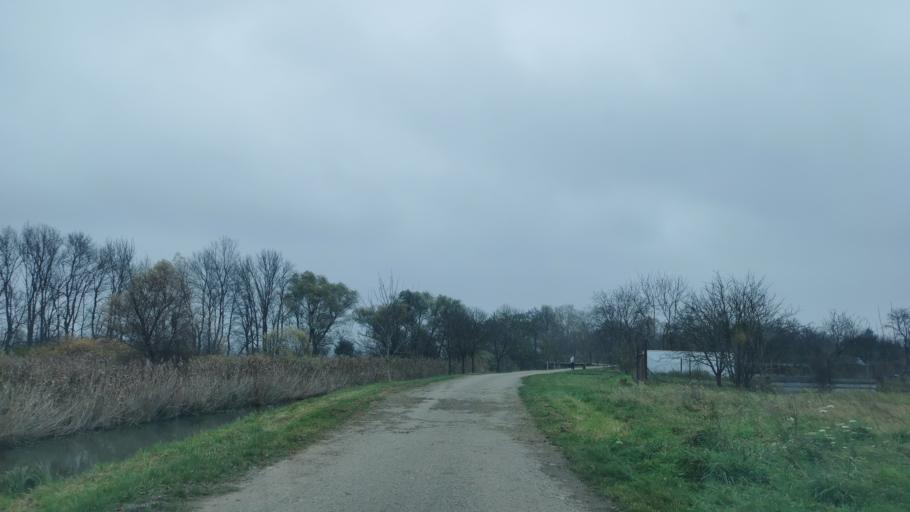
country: SK
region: Trnavsky
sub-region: Okres Skalica
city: Holic
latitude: 48.8331
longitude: 17.1668
